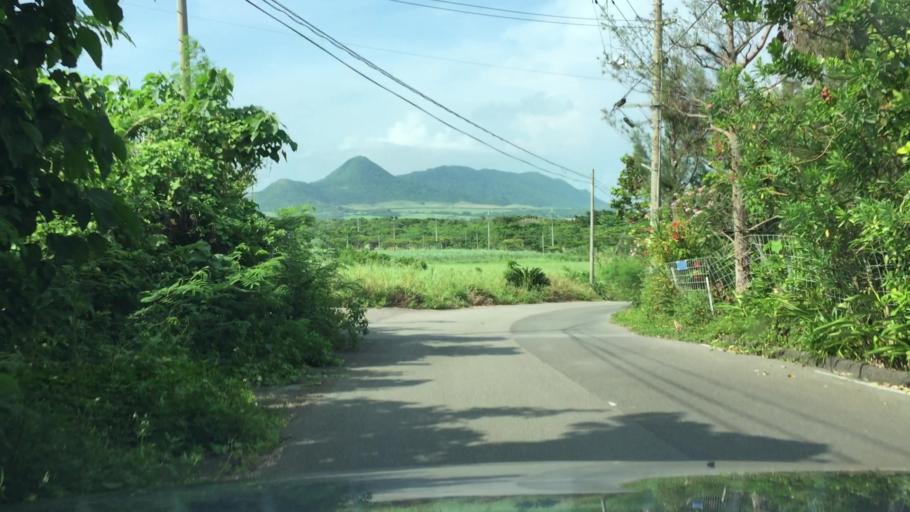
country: JP
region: Okinawa
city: Ishigaki
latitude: 24.4942
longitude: 124.2788
